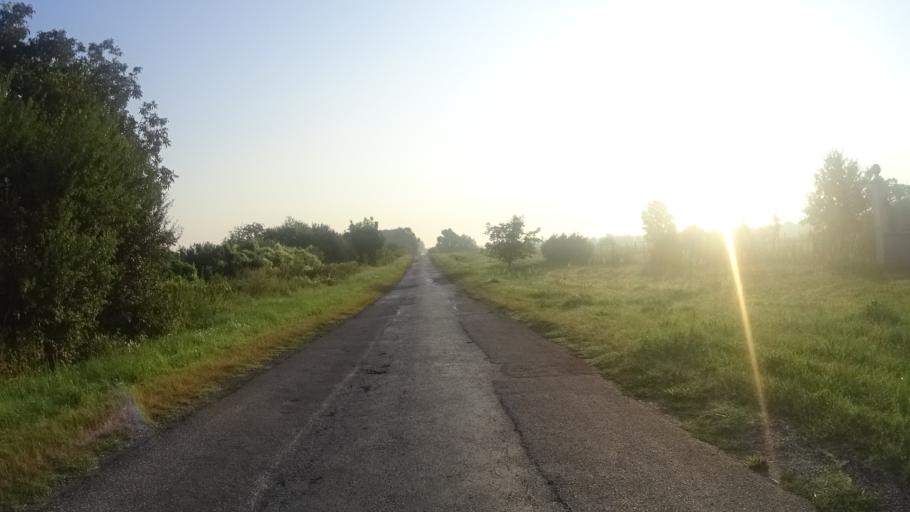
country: HU
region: Zala
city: Zalakomar
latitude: 46.5284
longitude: 17.1355
